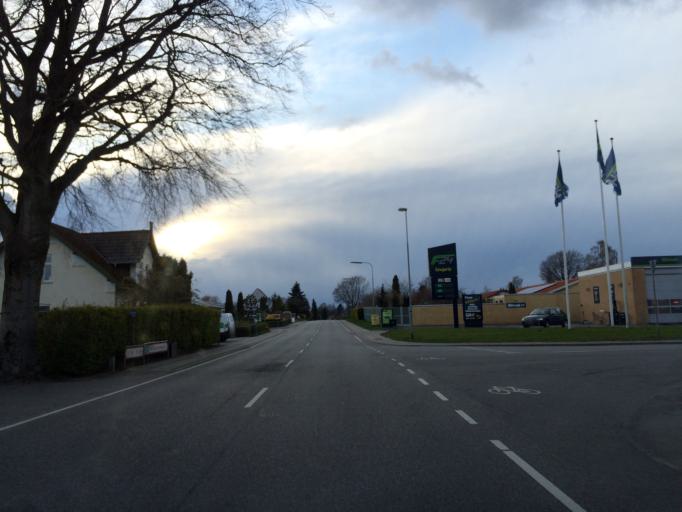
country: DK
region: South Denmark
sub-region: Odense Kommune
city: Bellinge
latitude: 55.3329
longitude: 10.3226
